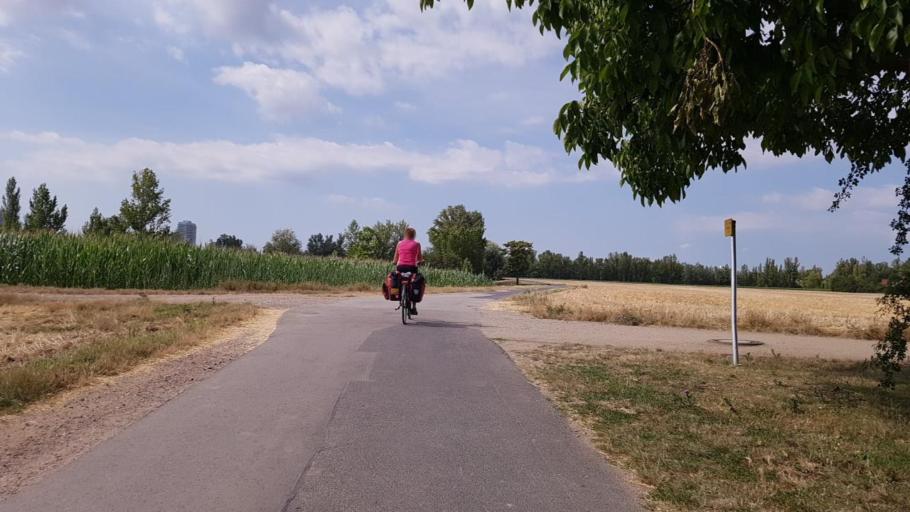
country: DE
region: Rheinland-Pfalz
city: Frankenthal
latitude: 49.5036
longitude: 8.3874
